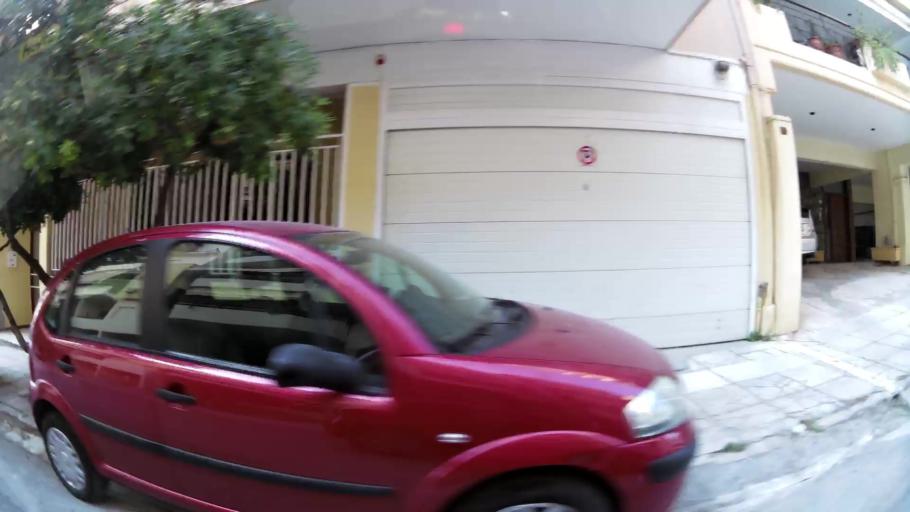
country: GR
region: Attica
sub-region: Nomarchia Athinas
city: Nea Smyrni
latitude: 37.9373
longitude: 23.7107
